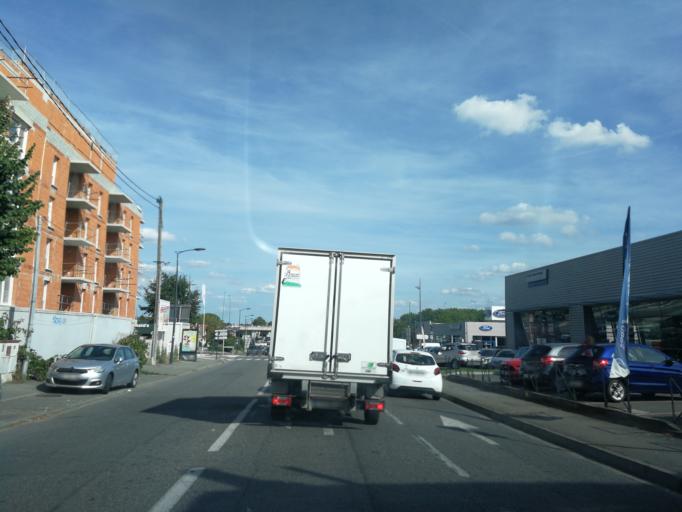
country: FR
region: Midi-Pyrenees
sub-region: Departement de la Haute-Garonne
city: Ramonville-Saint-Agne
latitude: 43.5734
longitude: 1.4924
